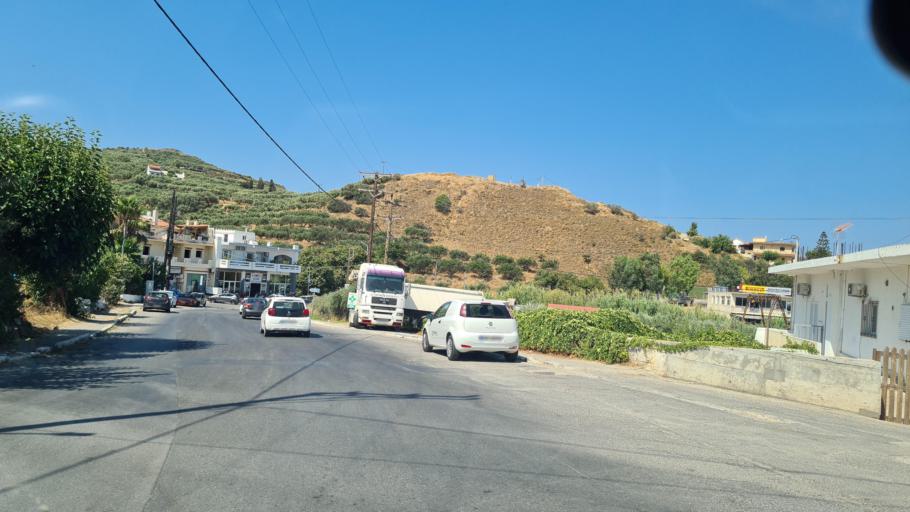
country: GR
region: Crete
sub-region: Nomos Chanias
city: Kissamos
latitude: 35.4916
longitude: 23.6659
